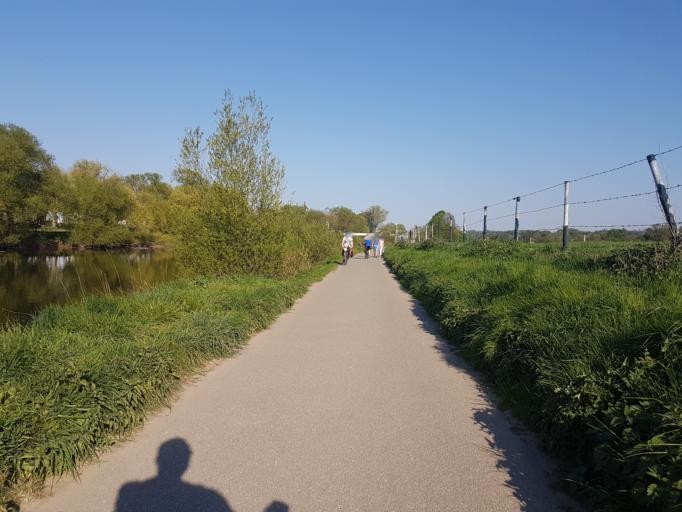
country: DE
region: North Rhine-Westphalia
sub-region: Regierungsbezirk Munster
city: Gelsenkirchen
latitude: 51.4296
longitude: 7.0932
